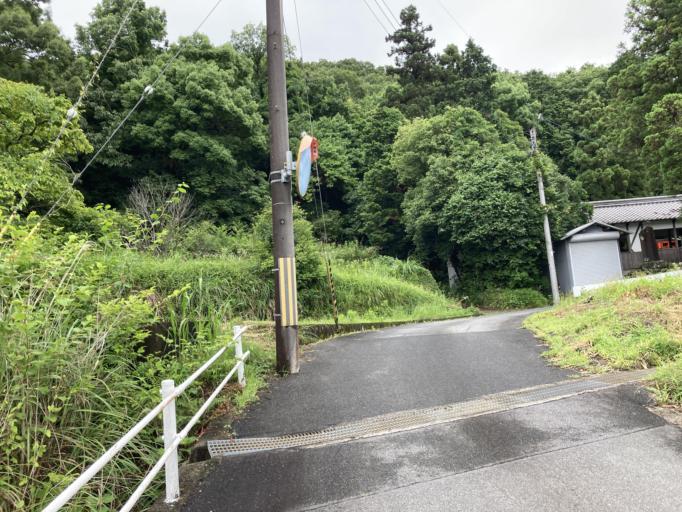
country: JP
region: Nara
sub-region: Ikoma-shi
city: Ikoma
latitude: 34.6242
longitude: 135.7108
